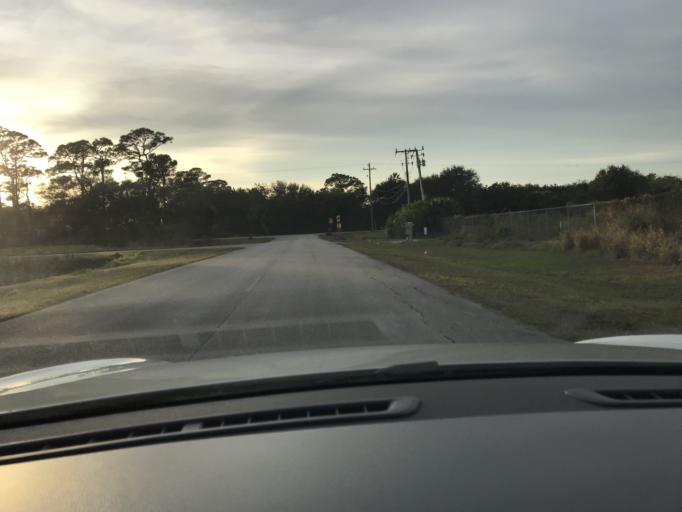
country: US
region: Florida
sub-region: Saint Lucie County
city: Lakewood Park
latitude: 27.4917
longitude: -80.3729
